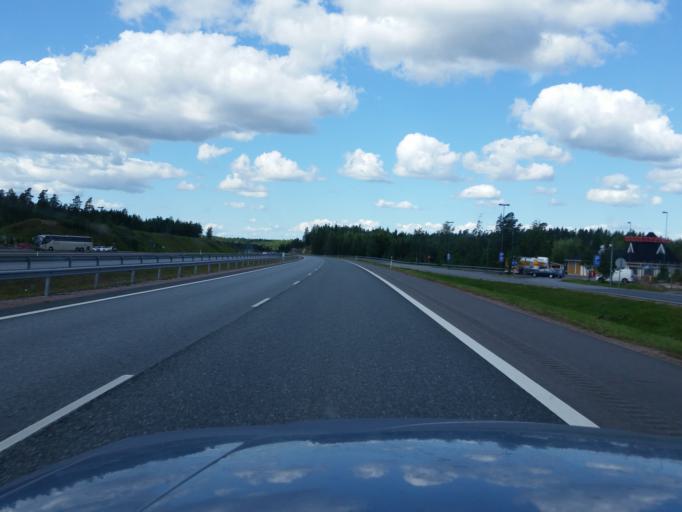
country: FI
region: Uusimaa
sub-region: Helsinki
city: Sammatti
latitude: 60.3686
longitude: 23.8637
